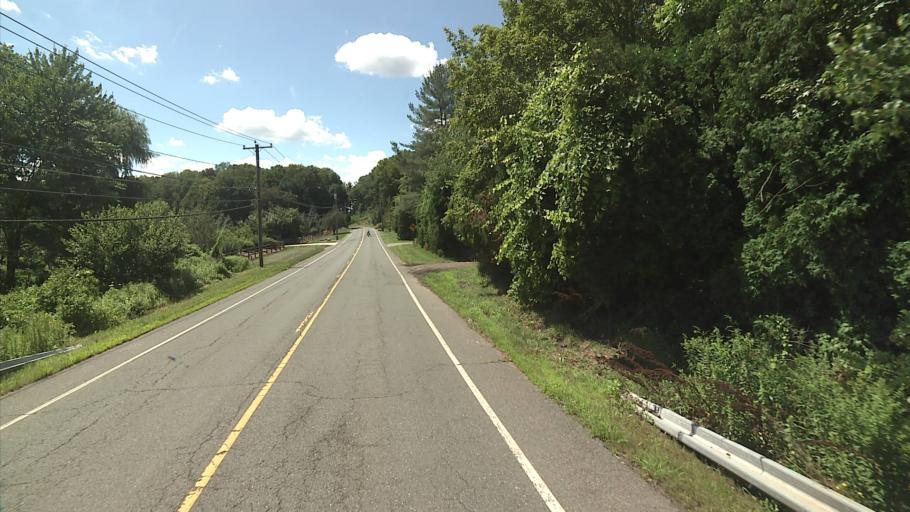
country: US
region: Massachusetts
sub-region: Hampden County
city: Southwick
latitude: 42.0206
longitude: -72.7329
